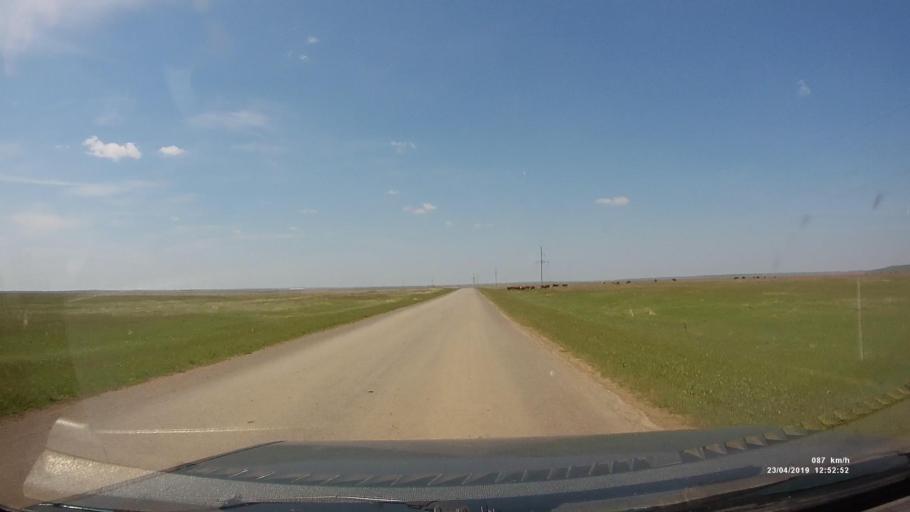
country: RU
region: Kalmykiya
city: Yashalta
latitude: 46.5688
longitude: 42.6039
